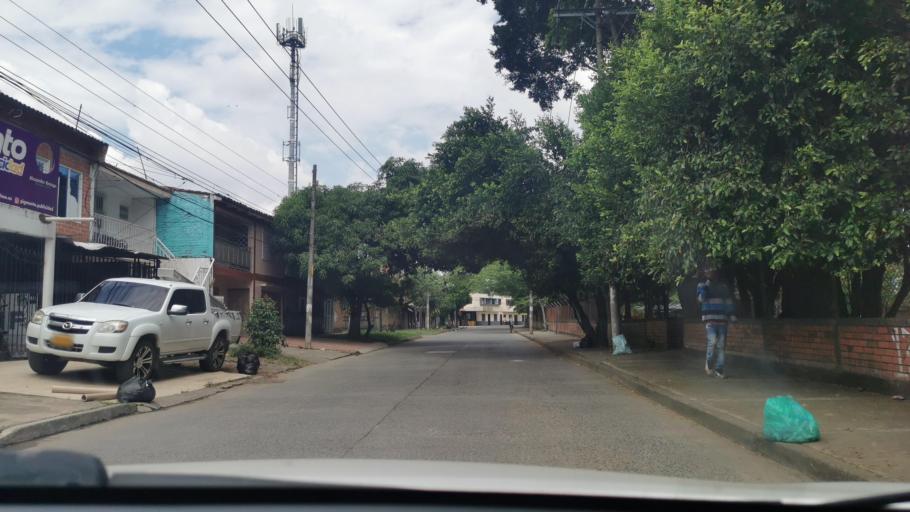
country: CO
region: Valle del Cauca
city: Jamundi
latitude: 3.2665
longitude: -76.5407
